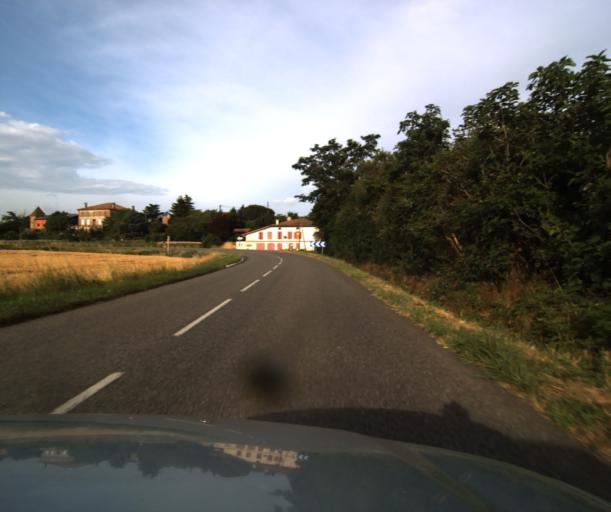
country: FR
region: Midi-Pyrenees
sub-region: Departement du Tarn-et-Garonne
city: Saint-Porquier
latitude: 43.9734
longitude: 1.1265
